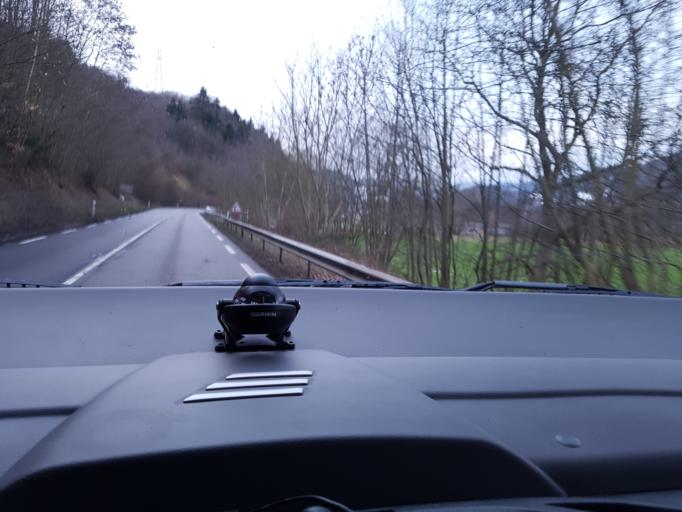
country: FR
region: Alsace
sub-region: Departement du Haut-Rhin
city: Liepvre
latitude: 48.2665
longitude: 7.3025
